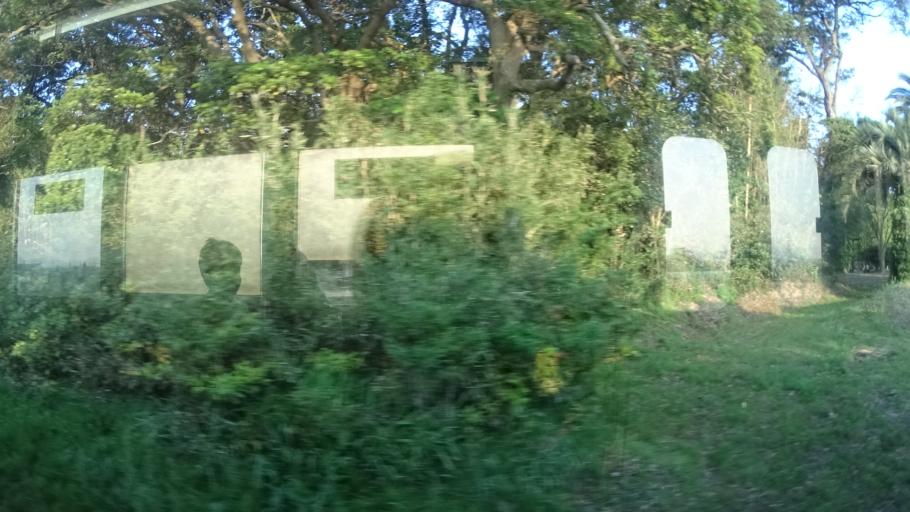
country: JP
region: Aichi
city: Tahara
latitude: 34.6795
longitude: 137.3205
